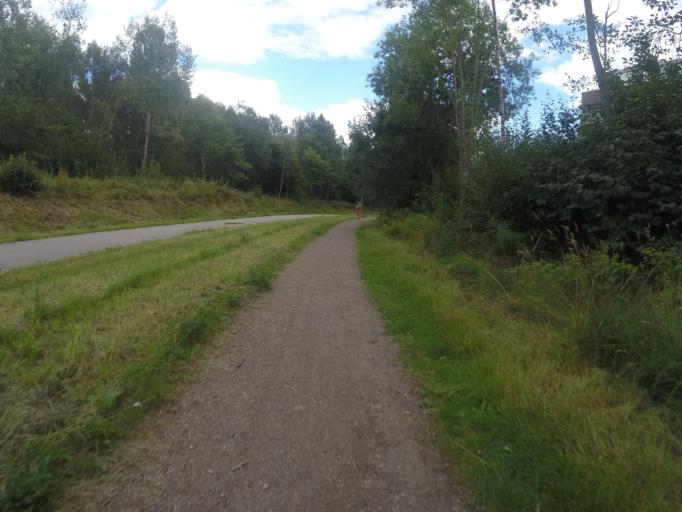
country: NO
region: Oslo
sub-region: Oslo
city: Oslo
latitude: 59.9698
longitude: 10.7736
